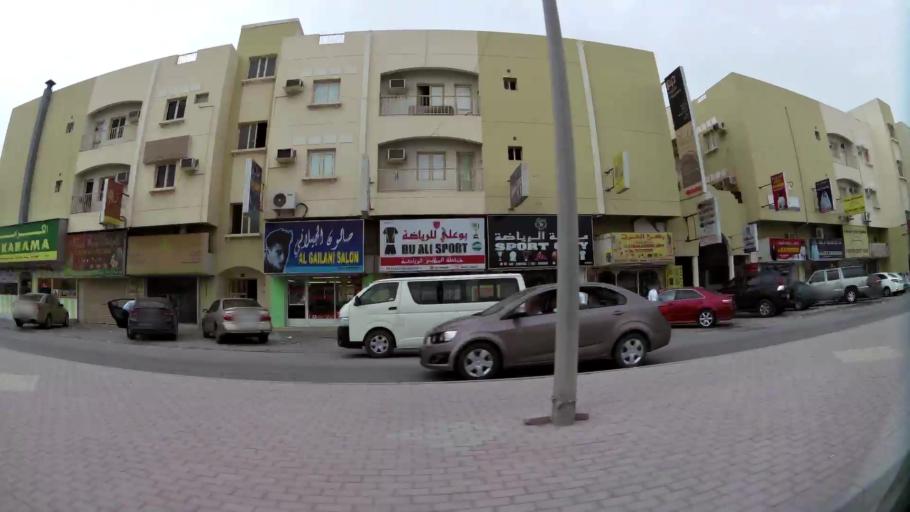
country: BH
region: Northern
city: Ar Rifa'
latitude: 26.1145
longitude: 50.5763
